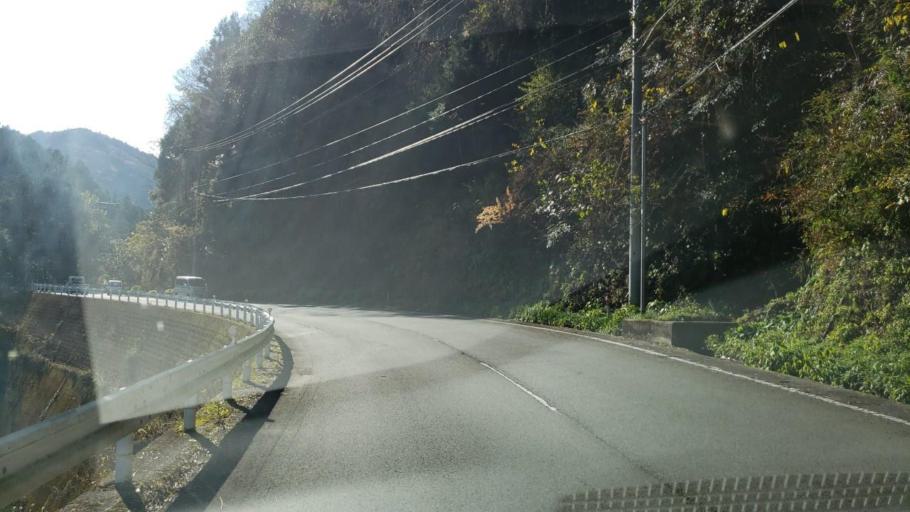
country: JP
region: Tokushima
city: Wakimachi
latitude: 34.0178
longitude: 134.0354
